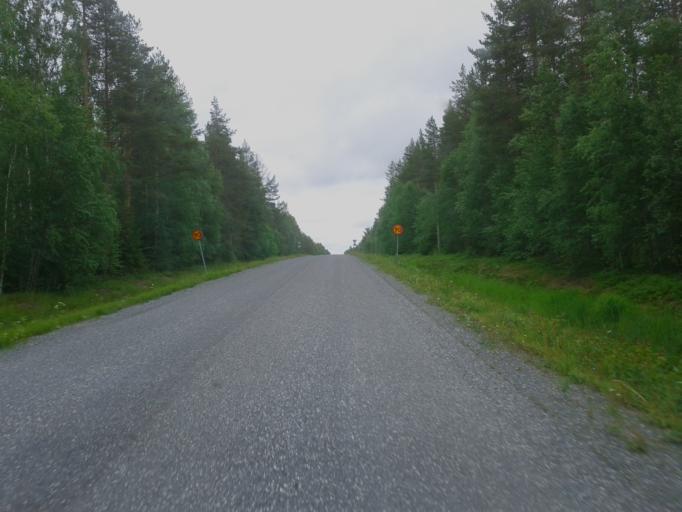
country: SE
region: Vaesterbotten
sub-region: Skelleftea Kommun
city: Storvik
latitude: 64.9869
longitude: 20.7107
